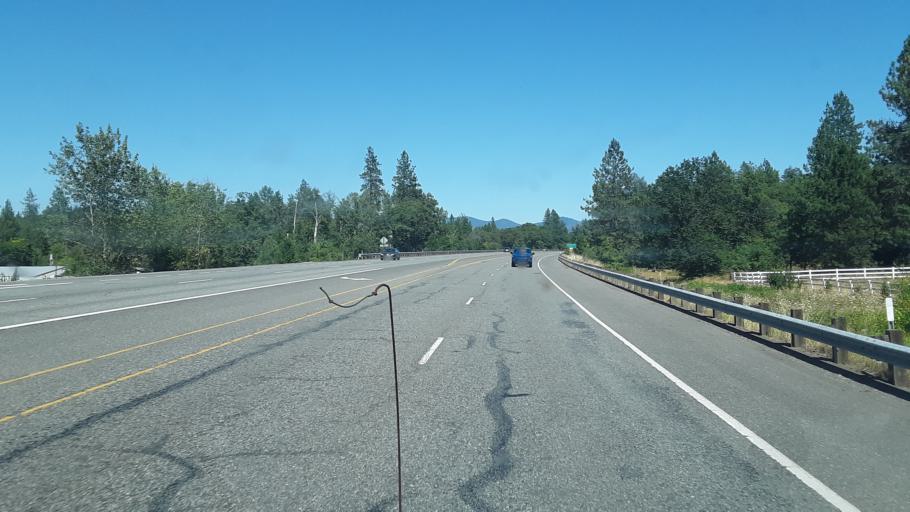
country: US
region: Oregon
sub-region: Josephine County
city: Redwood
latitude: 42.4093
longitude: -123.4332
